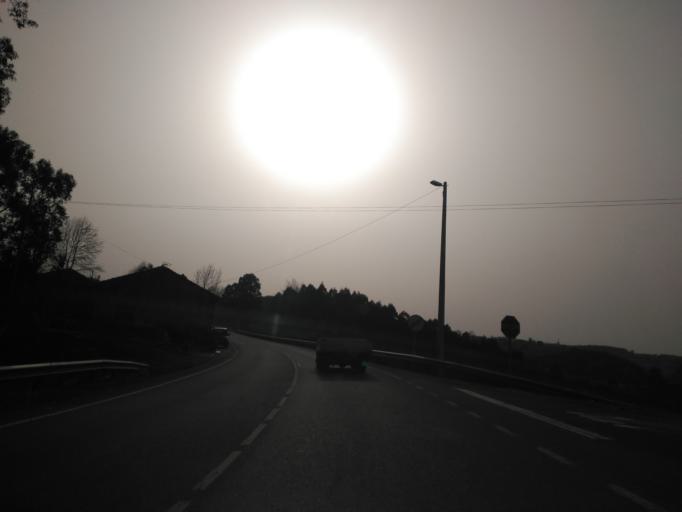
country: ES
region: Cantabria
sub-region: Provincia de Cantabria
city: Comillas
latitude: 43.3658
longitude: -4.2764
